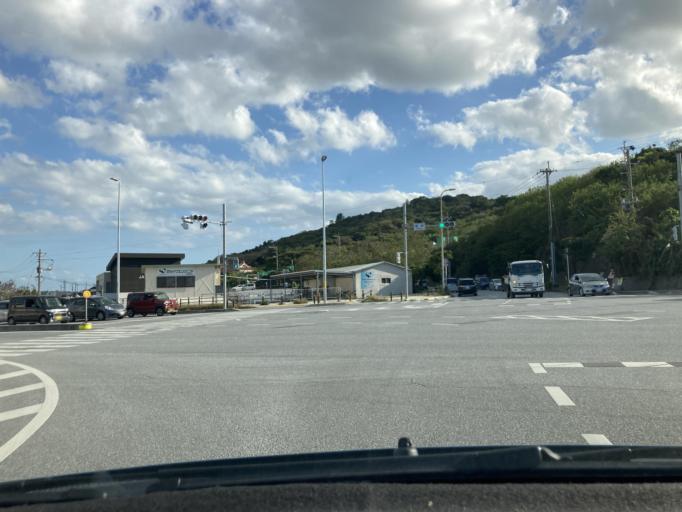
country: JP
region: Okinawa
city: Tomigusuku
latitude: 26.1918
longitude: 127.7031
